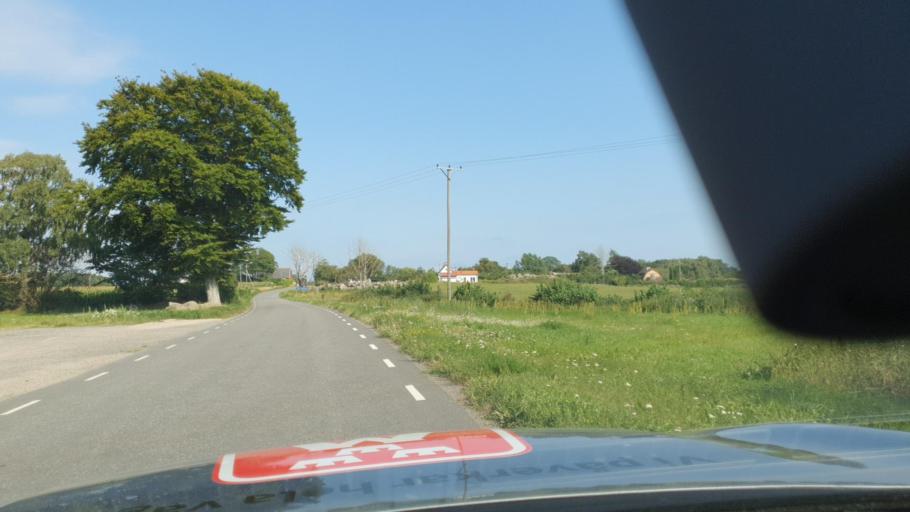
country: SE
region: Skane
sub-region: Bromolla Kommun
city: Bromoella
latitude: 56.0110
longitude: 14.4299
